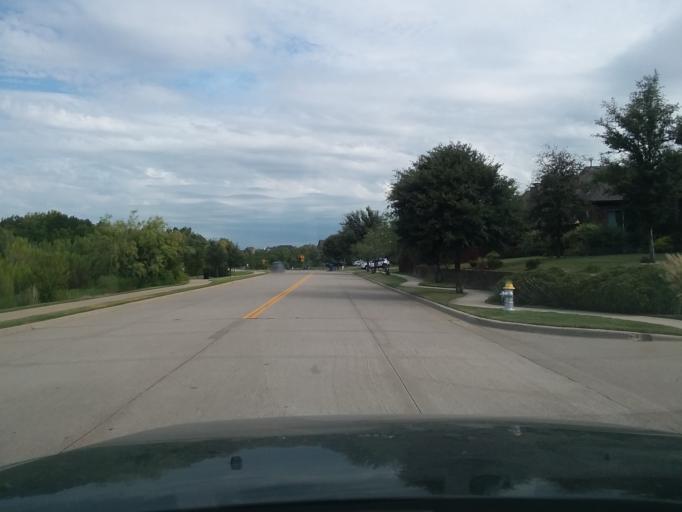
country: US
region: Texas
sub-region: Denton County
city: Copper Canyon
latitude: 33.1077
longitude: -97.1215
